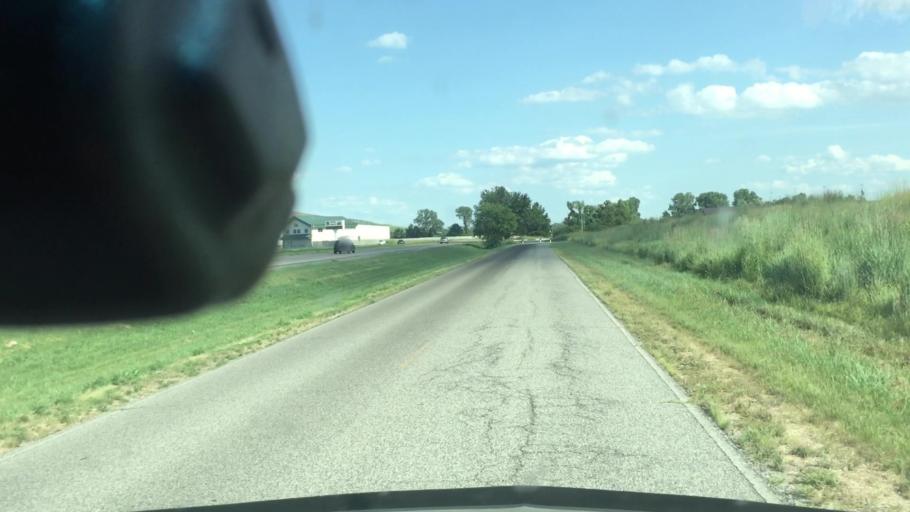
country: US
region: Illinois
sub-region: Madison County
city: Madison
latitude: 38.6617
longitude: -90.1401
